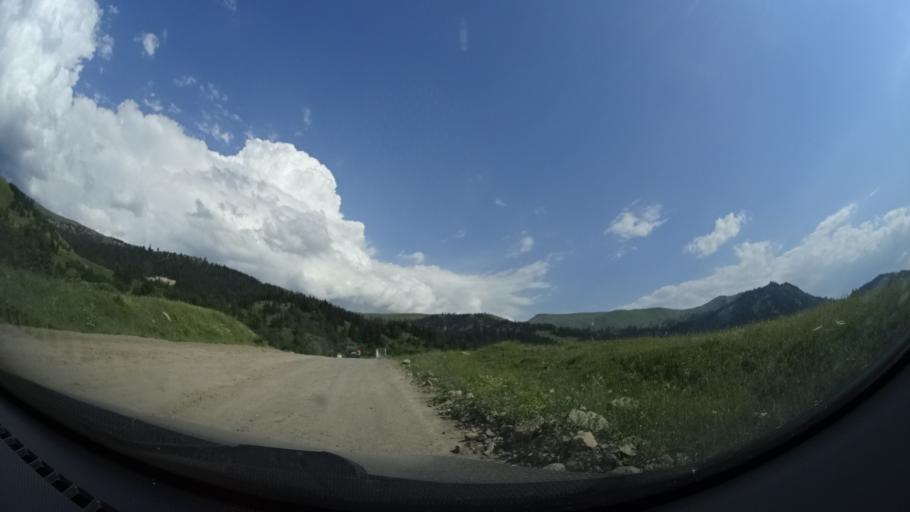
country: GE
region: Ajaria
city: Dioknisi
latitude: 41.6446
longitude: 42.4901
